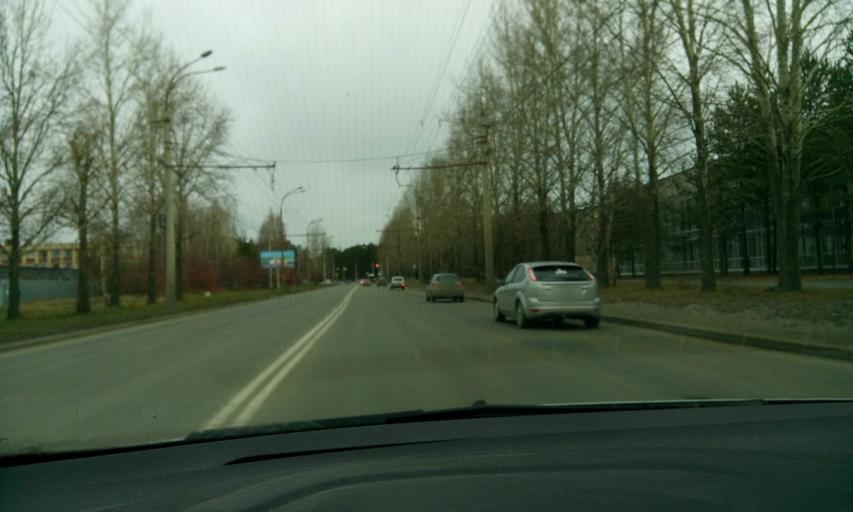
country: RU
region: Sverdlovsk
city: Sovkhoznyy
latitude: 56.7781
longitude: 60.5557
